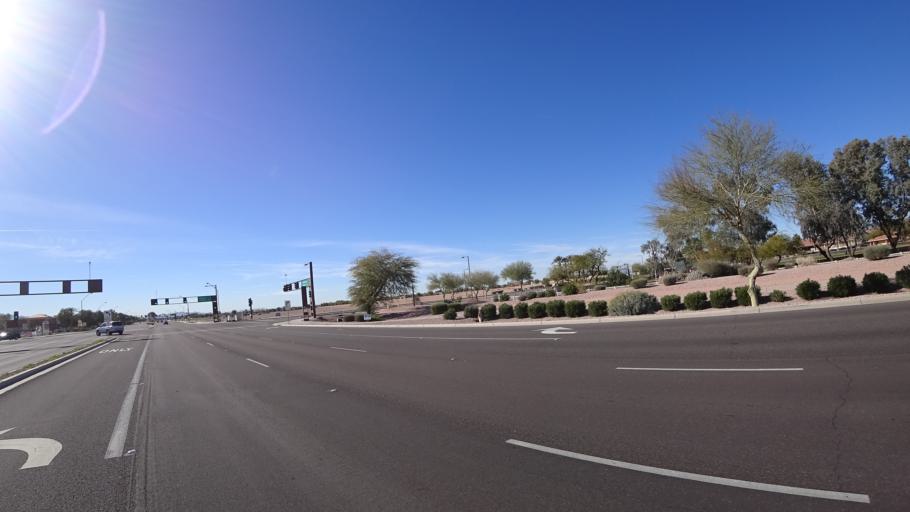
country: US
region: Arizona
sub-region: Maricopa County
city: Litchfield Park
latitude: 33.4762
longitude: -112.3926
